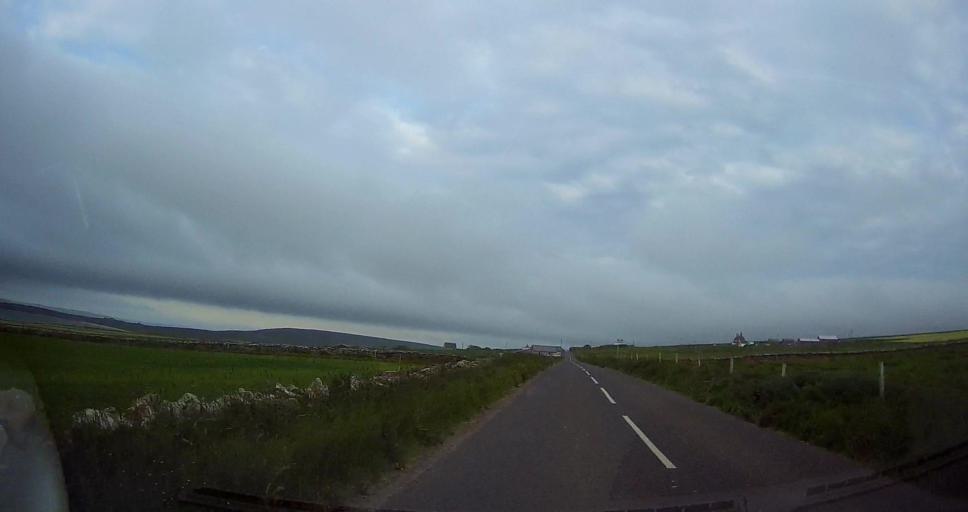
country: GB
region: Scotland
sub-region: Orkney Islands
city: Orkney
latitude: 59.1207
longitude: -3.1228
